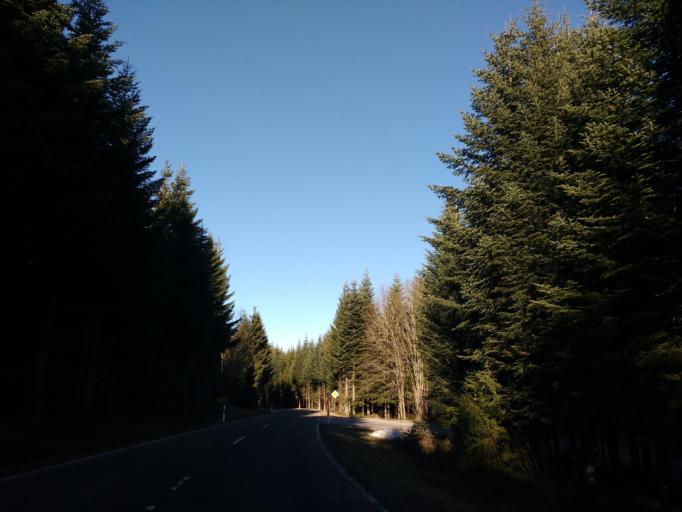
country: DE
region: Baden-Wuerttemberg
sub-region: Karlsruhe Region
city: Bad Rippoldsau-Schapbach
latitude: 48.4401
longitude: 8.3646
